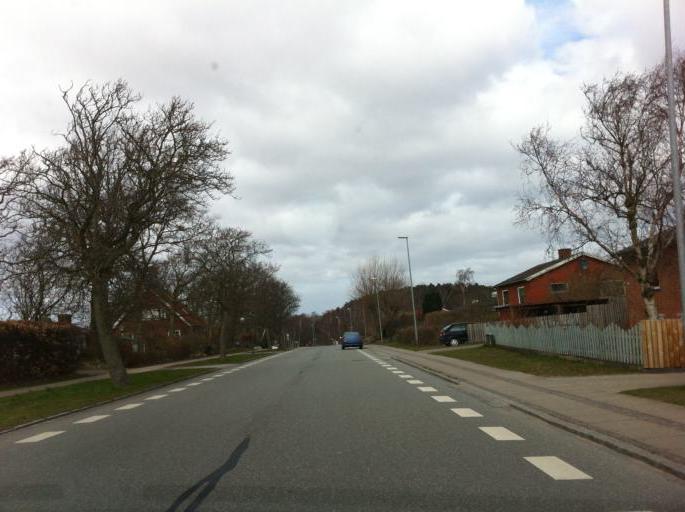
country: DK
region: Central Jutland
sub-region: Syddjurs Kommune
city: Ebeltoft
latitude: 56.2070
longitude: 10.6815
